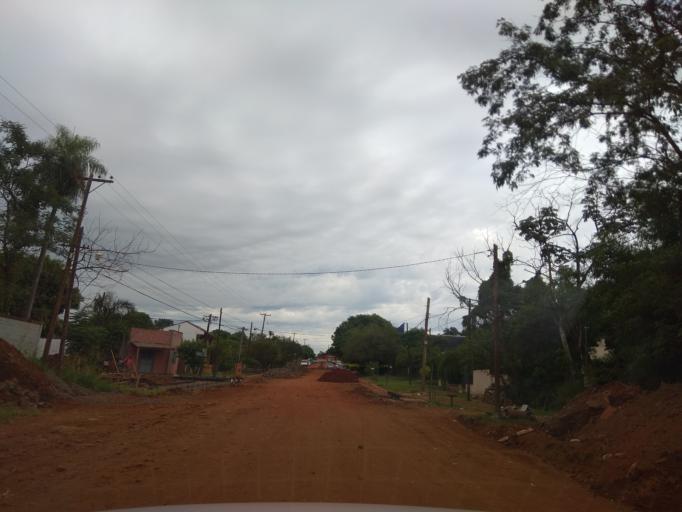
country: AR
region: Misiones
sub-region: Departamento de Capital
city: Posadas
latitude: -27.4098
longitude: -55.9086
